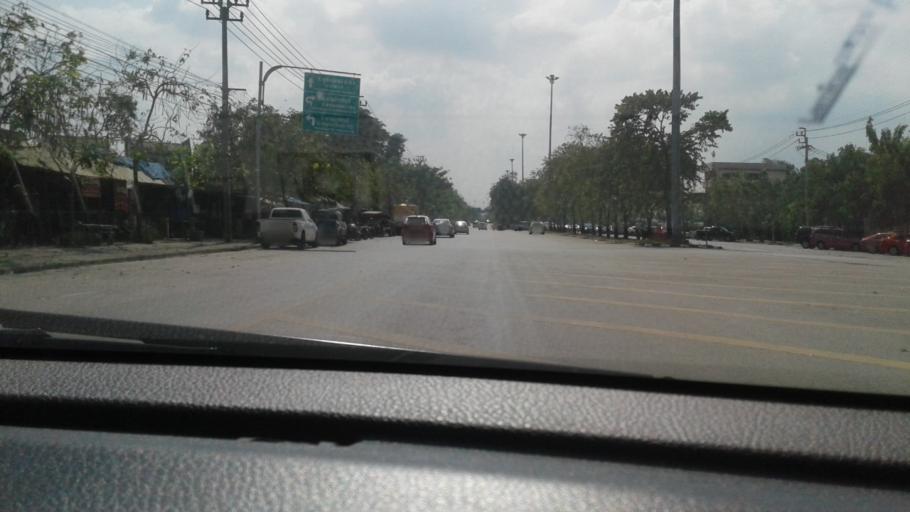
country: TH
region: Nonthaburi
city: Bang Yai
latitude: 13.7935
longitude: 100.3946
